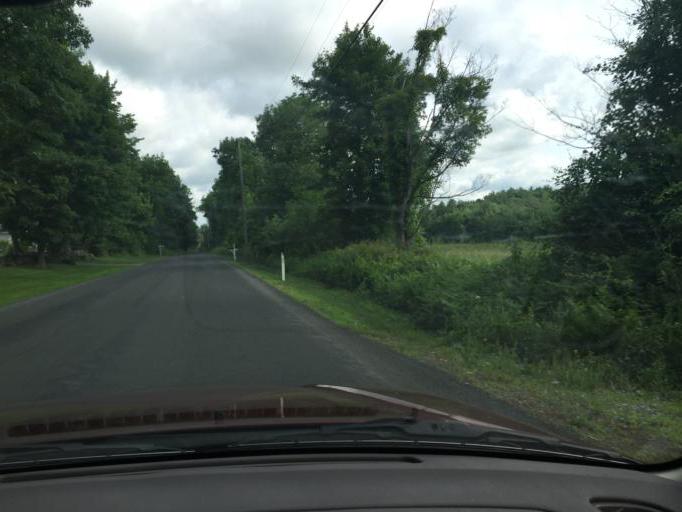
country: US
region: Connecticut
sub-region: Litchfield County
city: Litchfield
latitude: 41.7777
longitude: -73.2577
